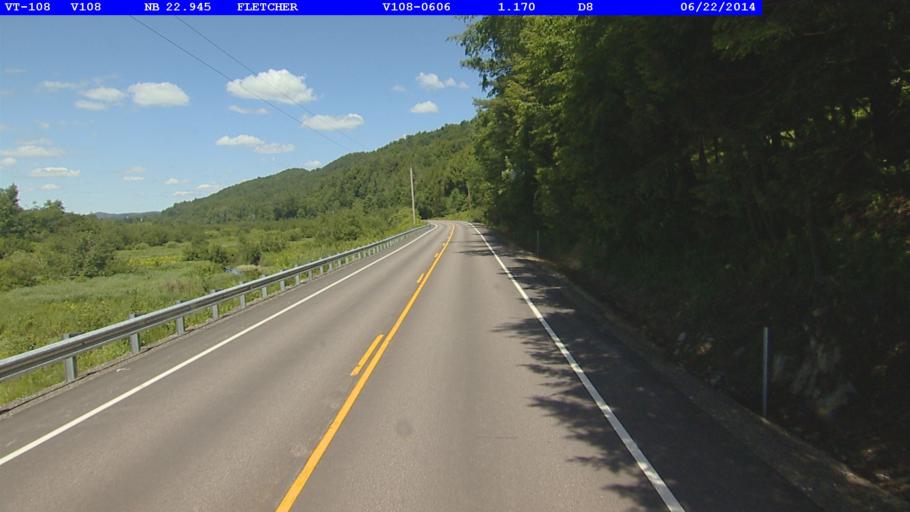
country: US
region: Vermont
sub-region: Lamoille County
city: Johnson
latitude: 44.7176
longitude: -72.8333
